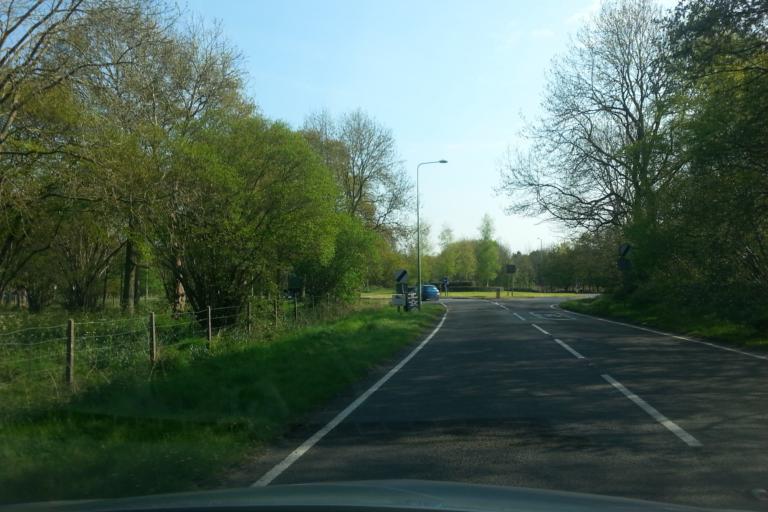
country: GB
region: England
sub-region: Suffolk
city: Wickham Market
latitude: 52.1296
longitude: 1.4231
